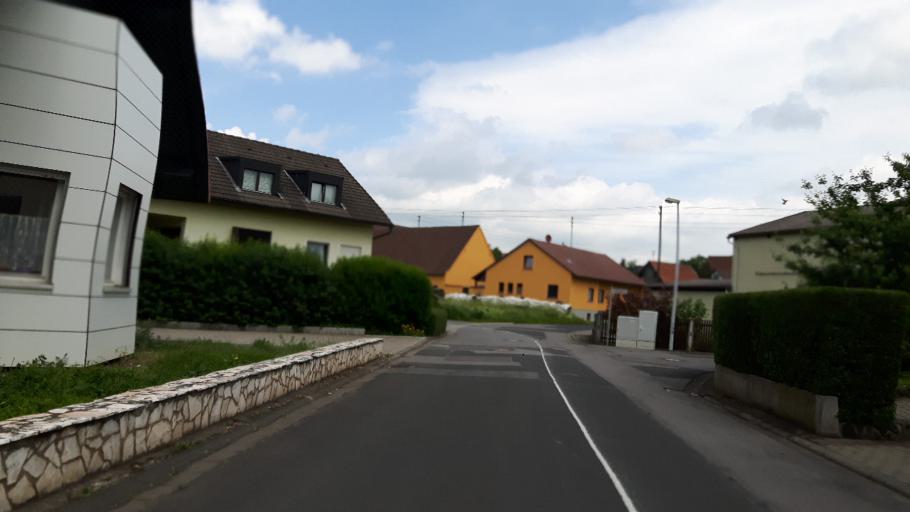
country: DE
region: Bavaria
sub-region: Regierungsbezirk Unterfranken
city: Trappstadt
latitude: 50.3195
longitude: 10.5688
